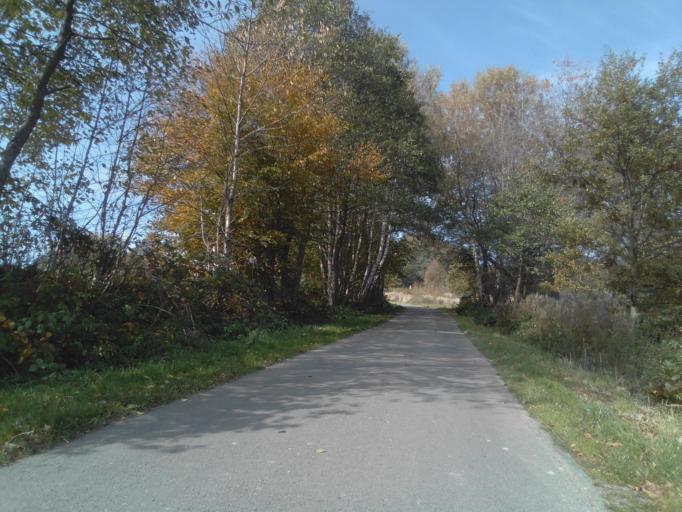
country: PL
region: Subcarpathian Voivodeship
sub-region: Powiat strzyzowski
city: Gwoznica Gorna
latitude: 49.8436
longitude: 21.9709
